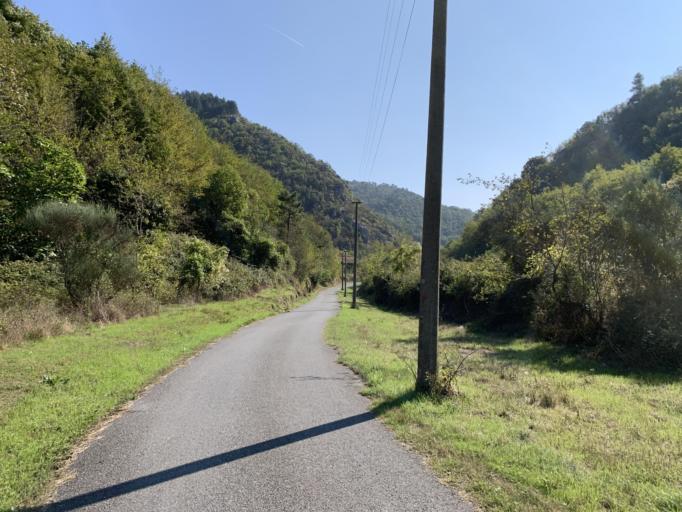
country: IT
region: Liguria
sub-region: Provincia di Savona
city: Magliolo
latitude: 44.2032
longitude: 8.2177
